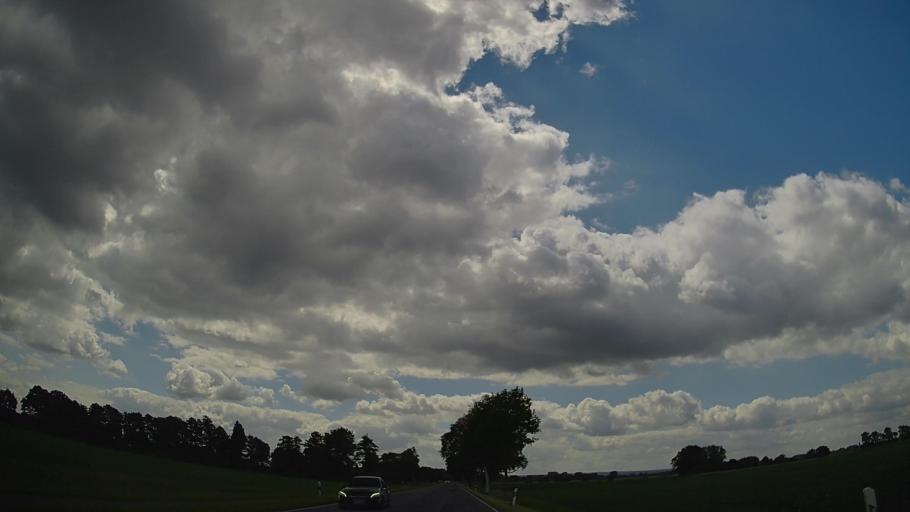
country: DE
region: Lower Saxony
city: Lembruch
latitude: 52.5514
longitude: 8.3678
